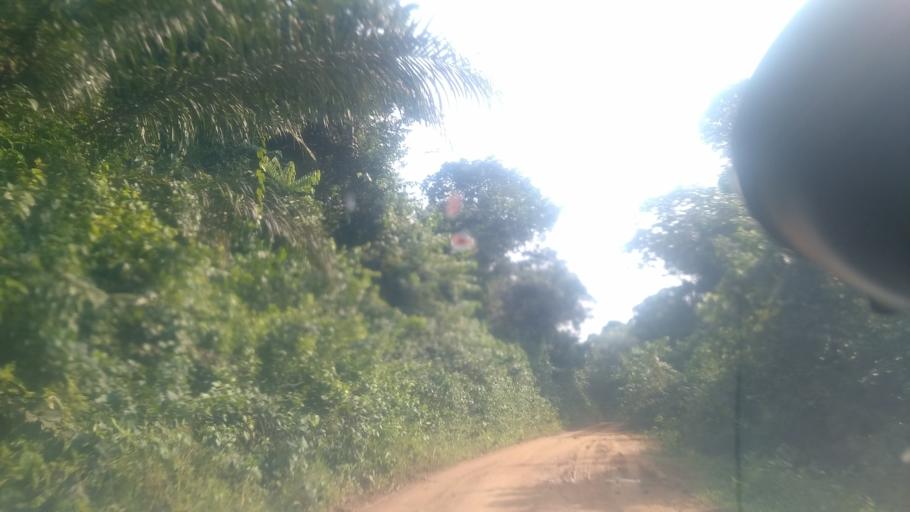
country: CM
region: South Province
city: Kribi
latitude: 2.6492
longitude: 9.8493
